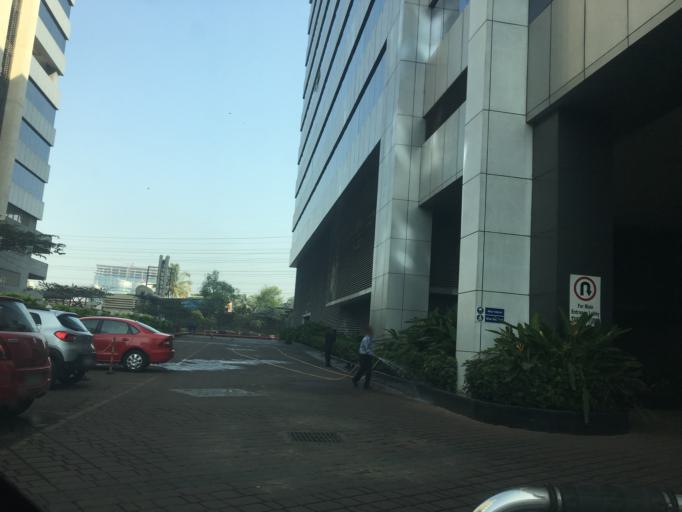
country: IN
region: Maharashtra
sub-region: Thane
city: Airoli
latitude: 19.1629
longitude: 73.0033
